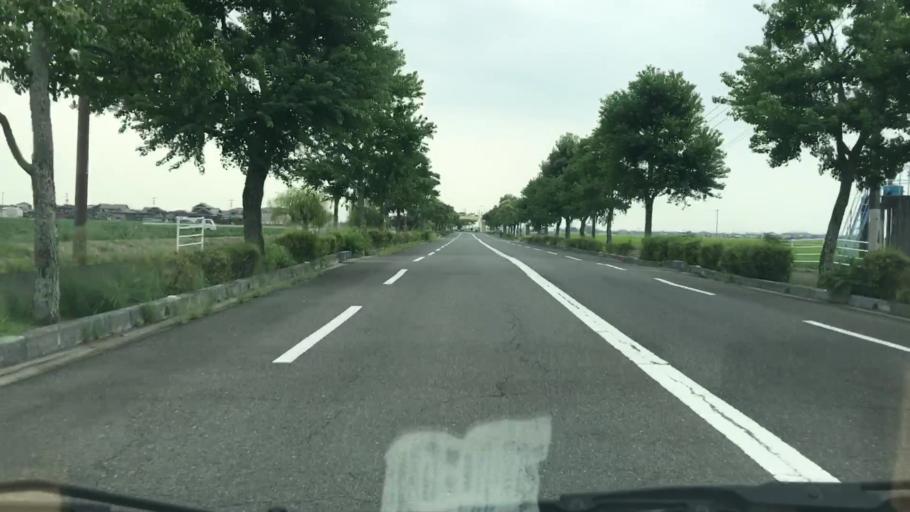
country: JP
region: Saga Prefecture
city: Saga-shi
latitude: 33.2106
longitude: 130.3042
